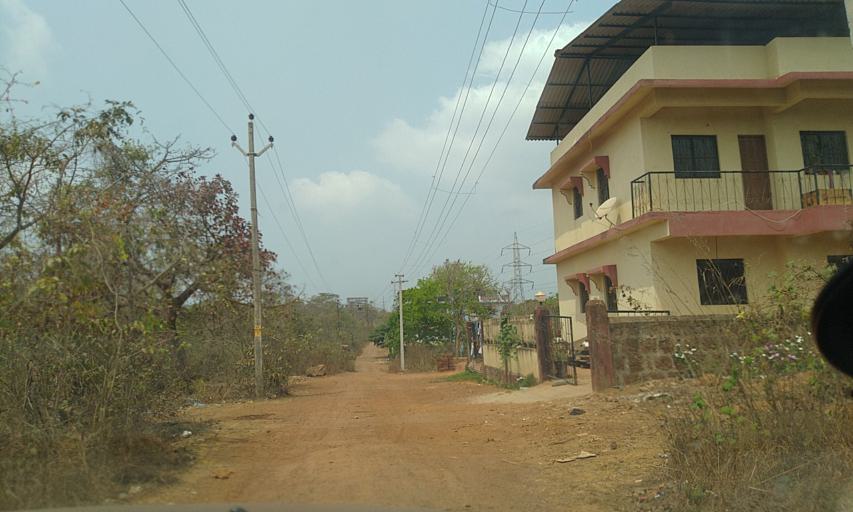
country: IN
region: Goa
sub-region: North Goa
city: Goa Velha
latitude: 15.4860
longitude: 73.9167
